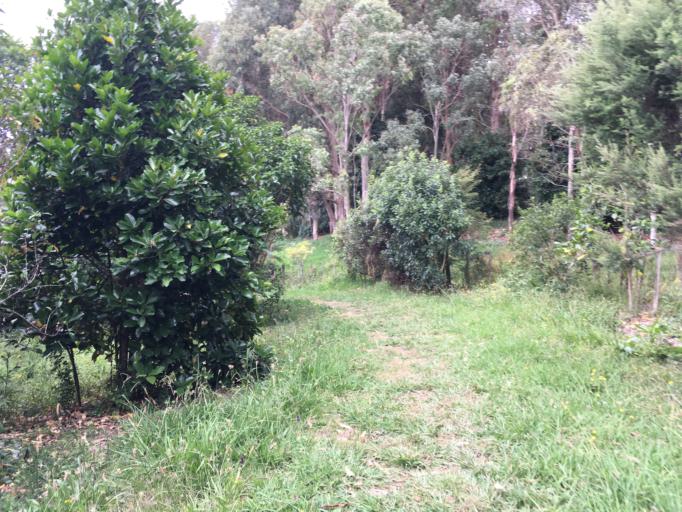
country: NZ
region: Auckland
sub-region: Auckland
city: Pakuranga
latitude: -36.7959
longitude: 175.0292
